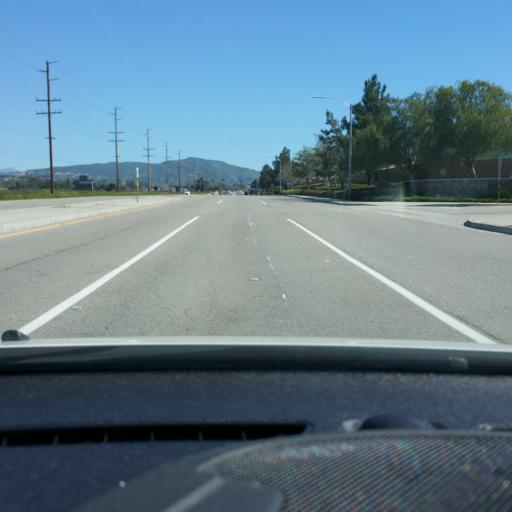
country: US
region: California
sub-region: Riverside County
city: Temecula
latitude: 33.4870
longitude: -117.0752
